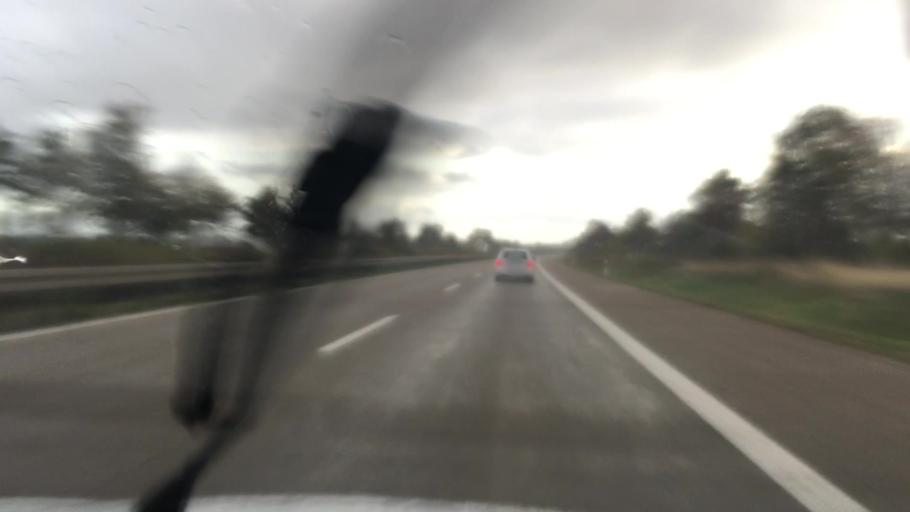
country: DE
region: Saxony-Anhalt
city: Glothe
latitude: 51.9164
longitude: 11.6990
